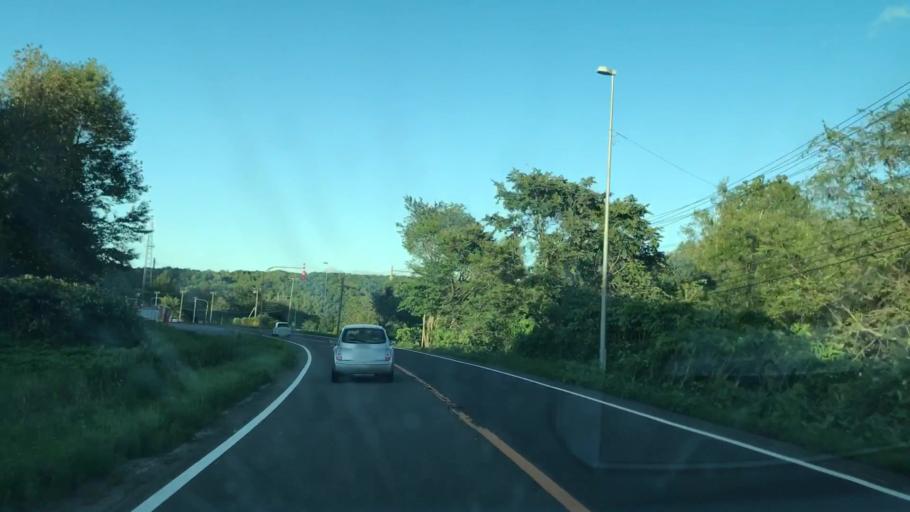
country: JP
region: Hokkaido
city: Niseko Town
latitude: 42.7562
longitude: 140.9243
